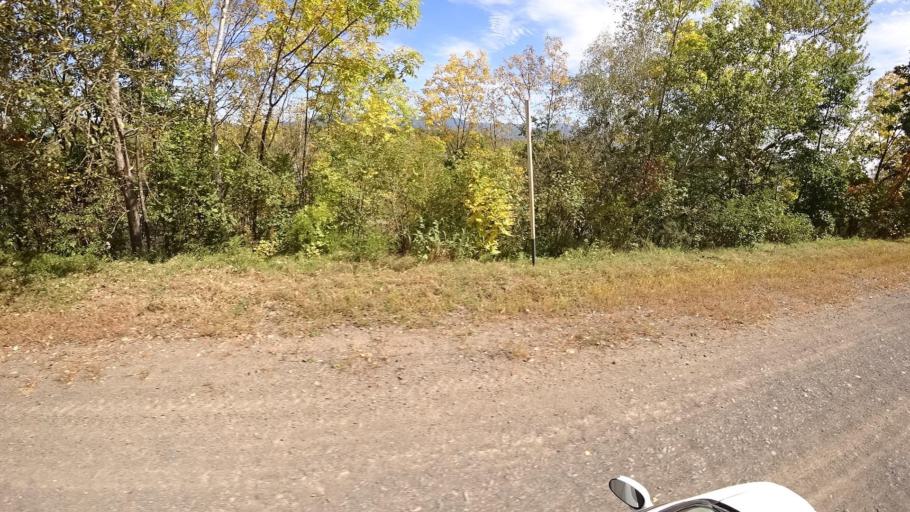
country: RU
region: Primorskiy
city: Yakovlevka
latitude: 44.6998
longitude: 133.6530
